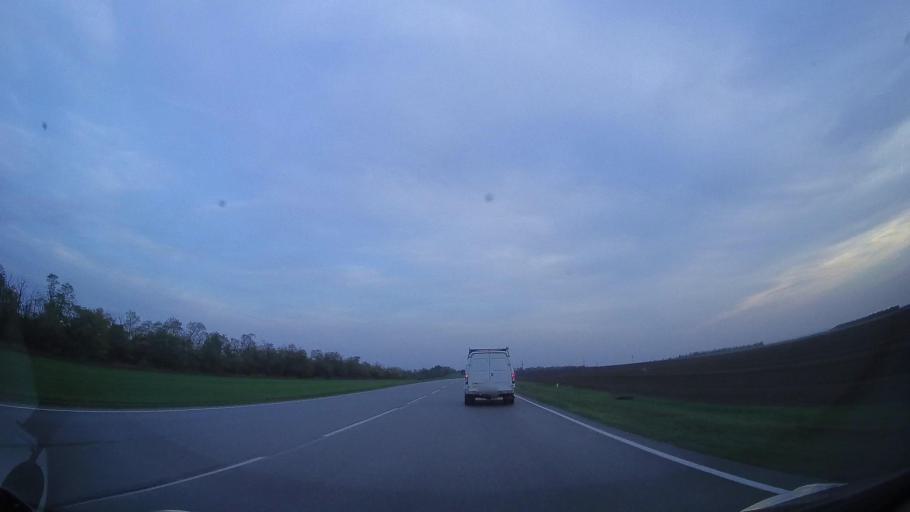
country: RU
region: Rostov
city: Kagal'nitskaya
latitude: 46.8994
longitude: 40.1242
